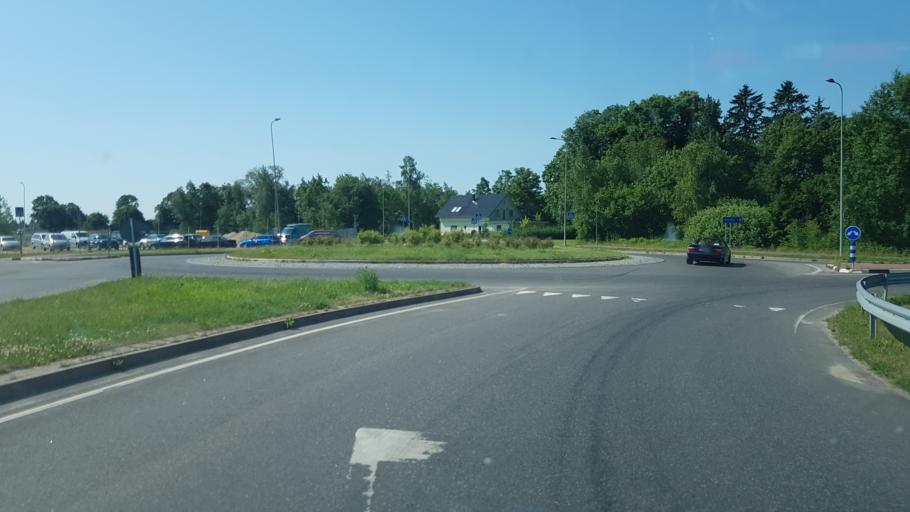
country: EE
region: Tartu
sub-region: UElenurme vald
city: Ulenurme
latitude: 58.3452
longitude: 26.6996
